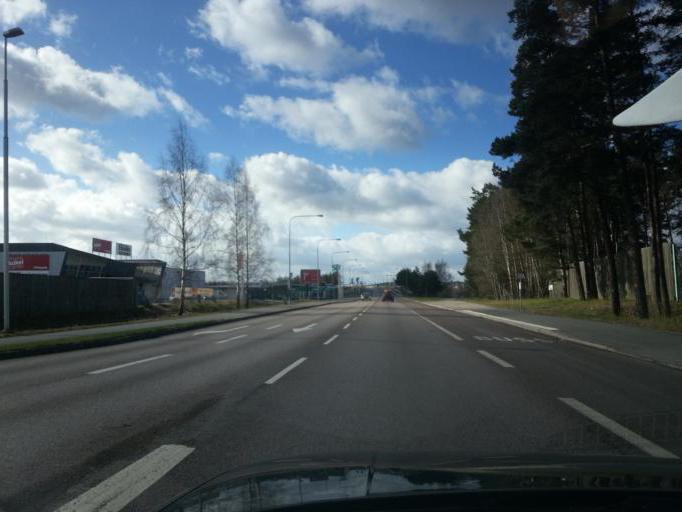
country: SE
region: Joenkoeping
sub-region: Jonkopings Kommun
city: Jonkoping
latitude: 57.7675
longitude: 14.1709
